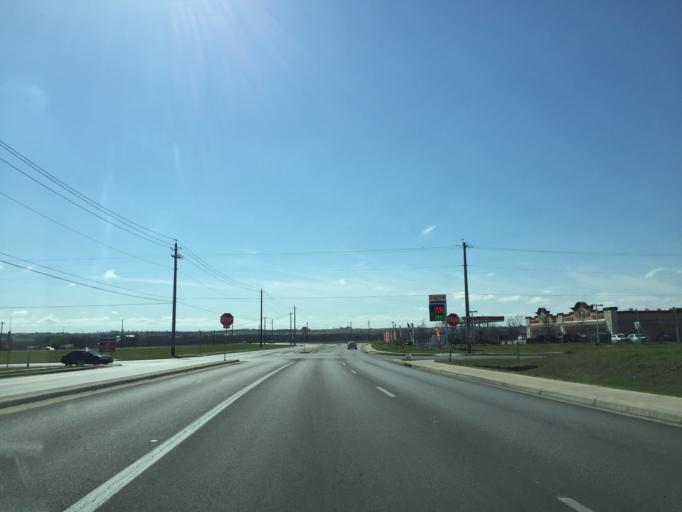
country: US
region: Texas
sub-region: Travis County
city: Garfield
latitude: 30.1568
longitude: -97.6414
